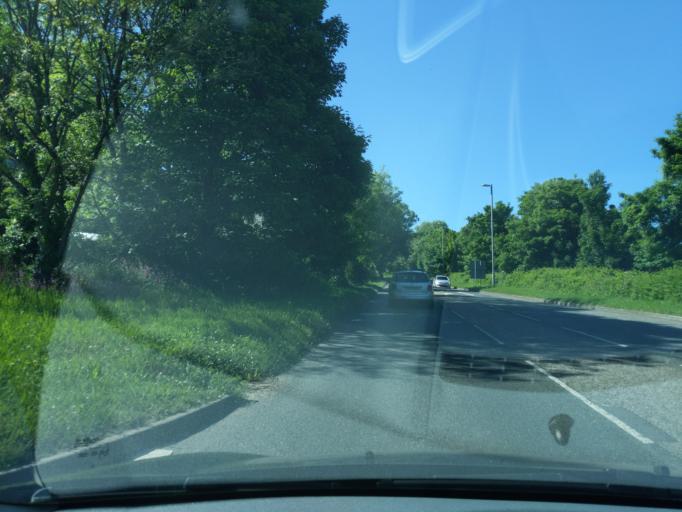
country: GB
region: England
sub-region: Cornwall
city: Helston
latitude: 50.1020
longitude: -5.2817
